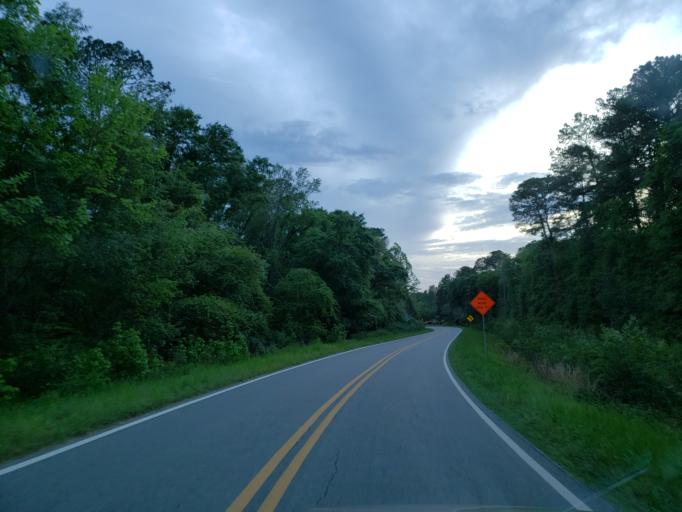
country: US
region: Georgia
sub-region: Lowndes County
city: Hahira
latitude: 30.9491
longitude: -83.3840
